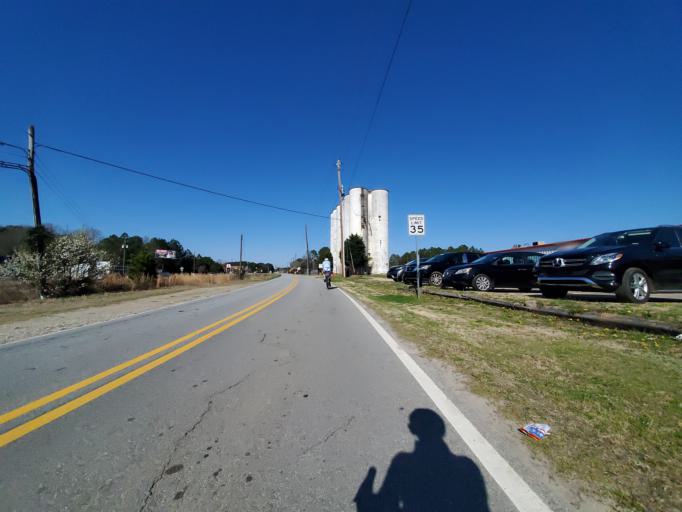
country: US
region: Georgia
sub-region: Clarke County
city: Country Club Estates
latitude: 33.9885
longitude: -83.4226
